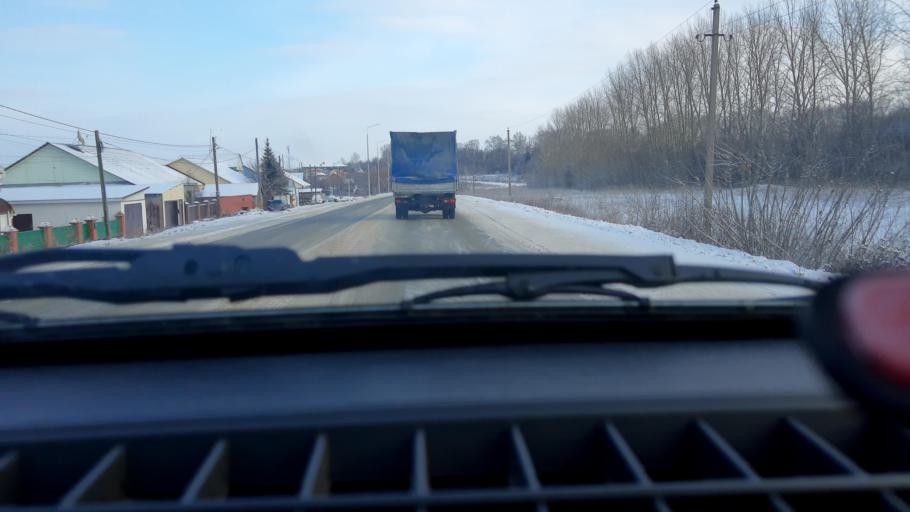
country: RU
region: Bashkortostan
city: Iglino
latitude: 54.7949
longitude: 56.2969
